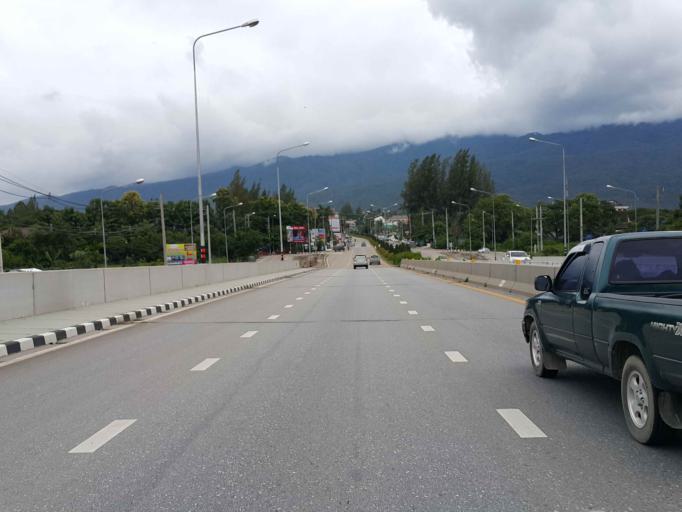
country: TH
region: Chiang Mai
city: Chiang Mai
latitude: 18.8438
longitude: 98.9844
